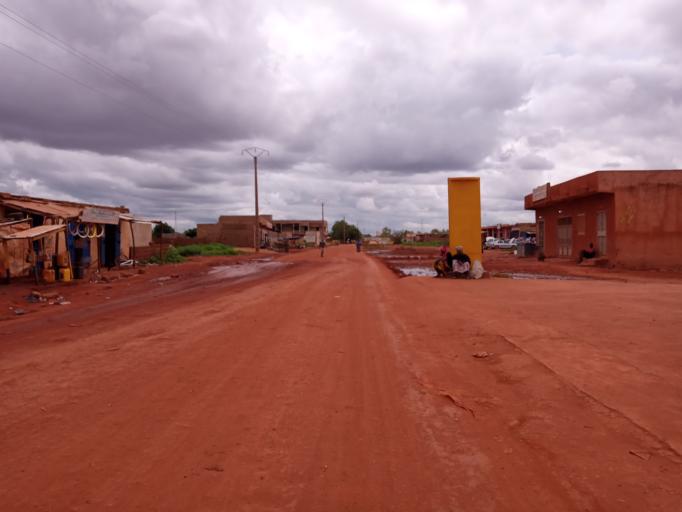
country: ML
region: Bamako
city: Bamako
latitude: 12.5403
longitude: -7.9944
